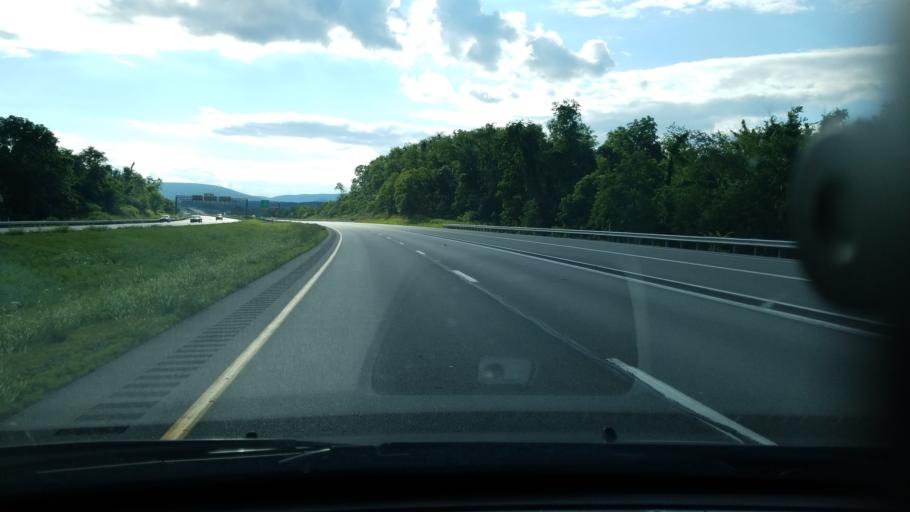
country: US
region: Pennsylvania
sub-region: Union County
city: New Columbia
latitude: 41.0512
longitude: -76.8451
